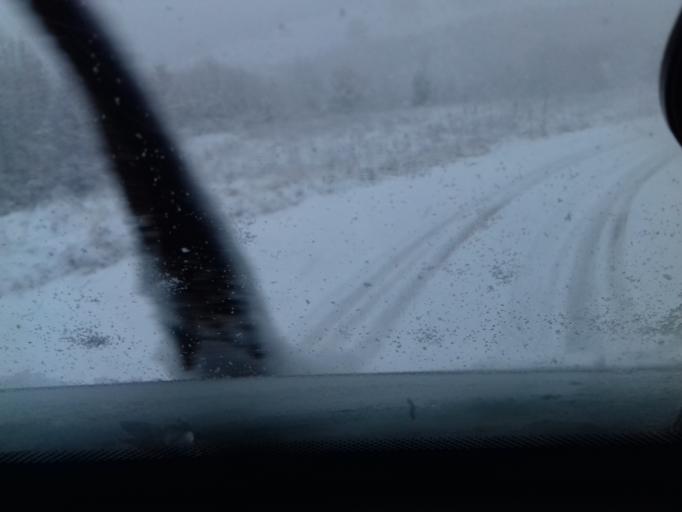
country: BA
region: Federation of Bosnia and Herzegovina
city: Lokvine
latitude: 44.2450
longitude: 17.8025
